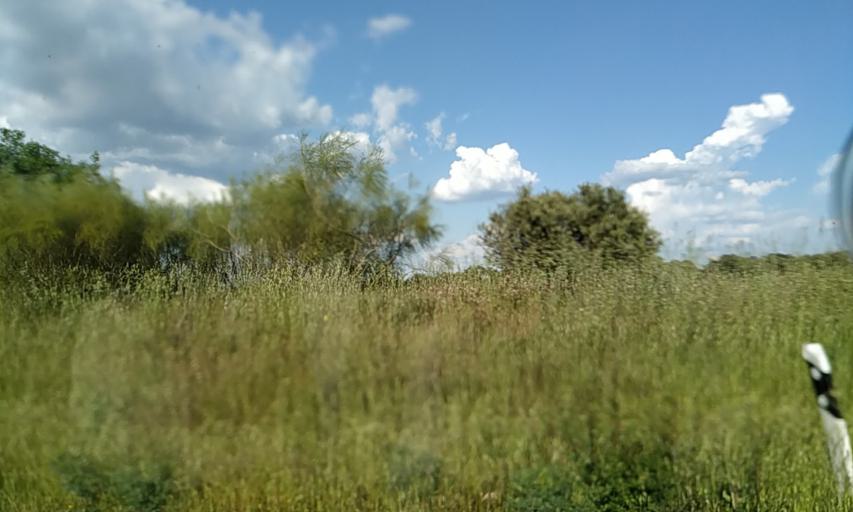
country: PT
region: Portalegre
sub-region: Portalegre
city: Urra
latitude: 39.1618
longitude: -7.4540
